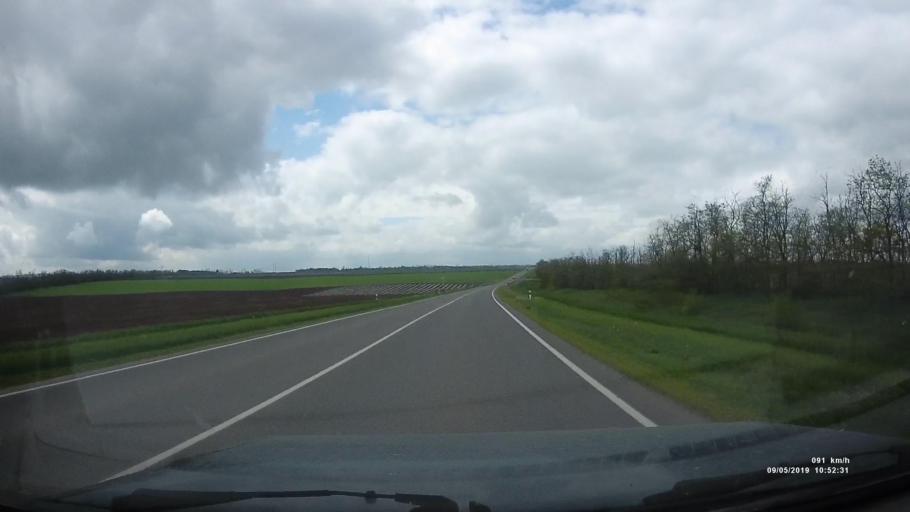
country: RU
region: Rostov
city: Peshkovo
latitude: 46.8998
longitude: 39.3524
